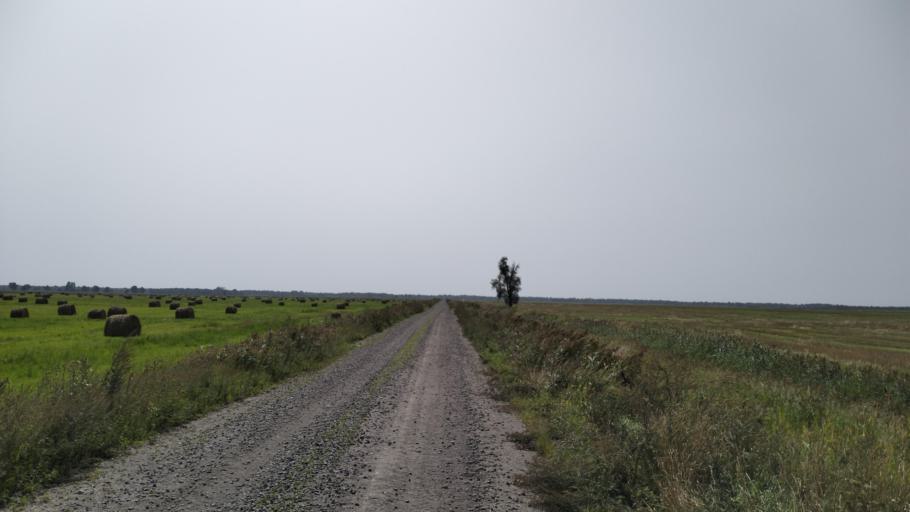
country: BY
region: Brest
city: Davyd-Haradok
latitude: 51.9950
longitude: 27.1764
